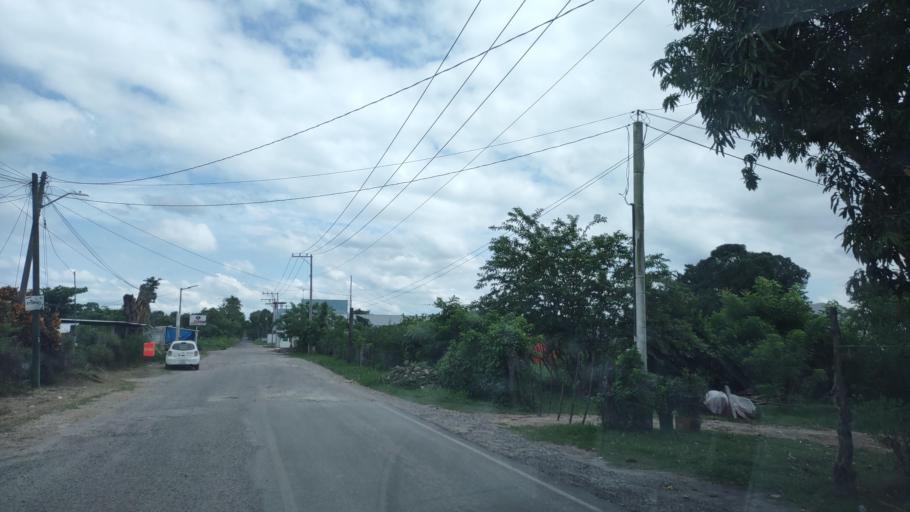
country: MX
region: Veracruz
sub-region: Martinez de la Torre
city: El Progreso
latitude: 20.0968
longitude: -97.0096
